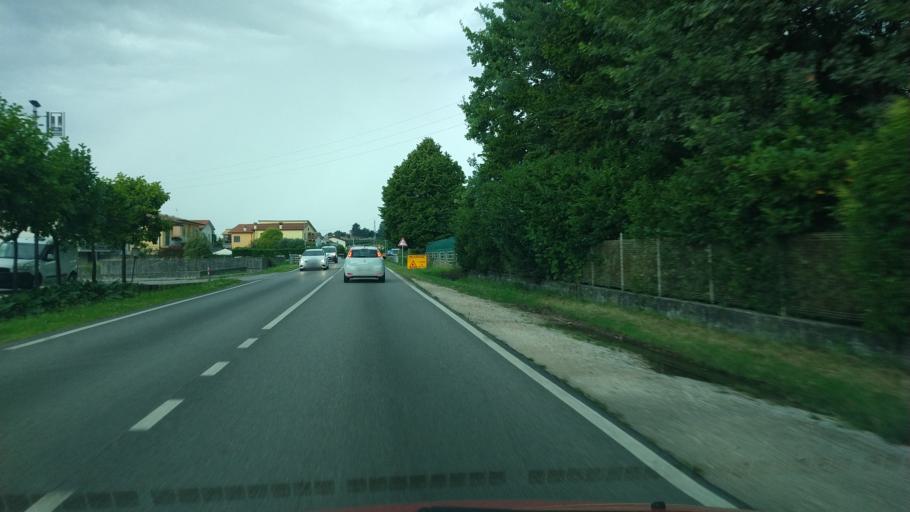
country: IT
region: Veneto
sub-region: Provincia di Vicenza
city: Zugliano
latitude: 45.7302
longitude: 11.5164
